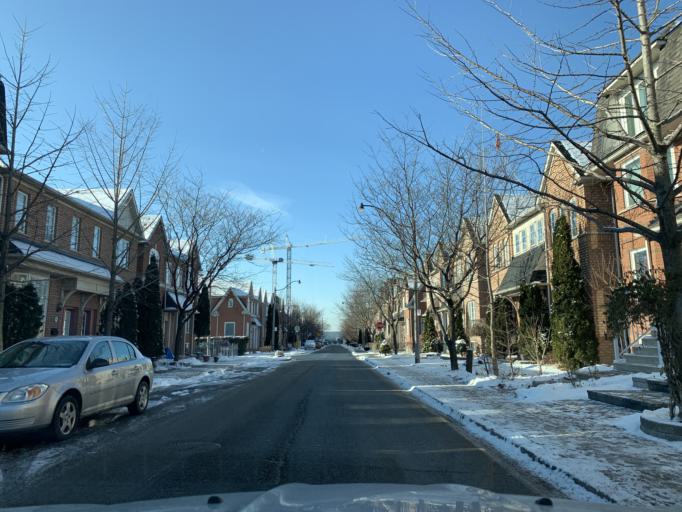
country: CA
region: Ontario
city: Toronto
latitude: 43.6717
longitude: -79.4748
